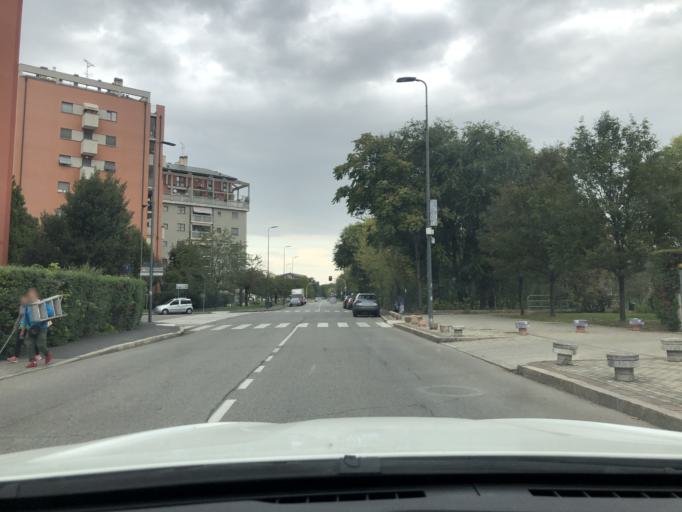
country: IT
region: Lombardy
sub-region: Citta metropolitana di Milano
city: Pero
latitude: 45.4924
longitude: 9.1144
